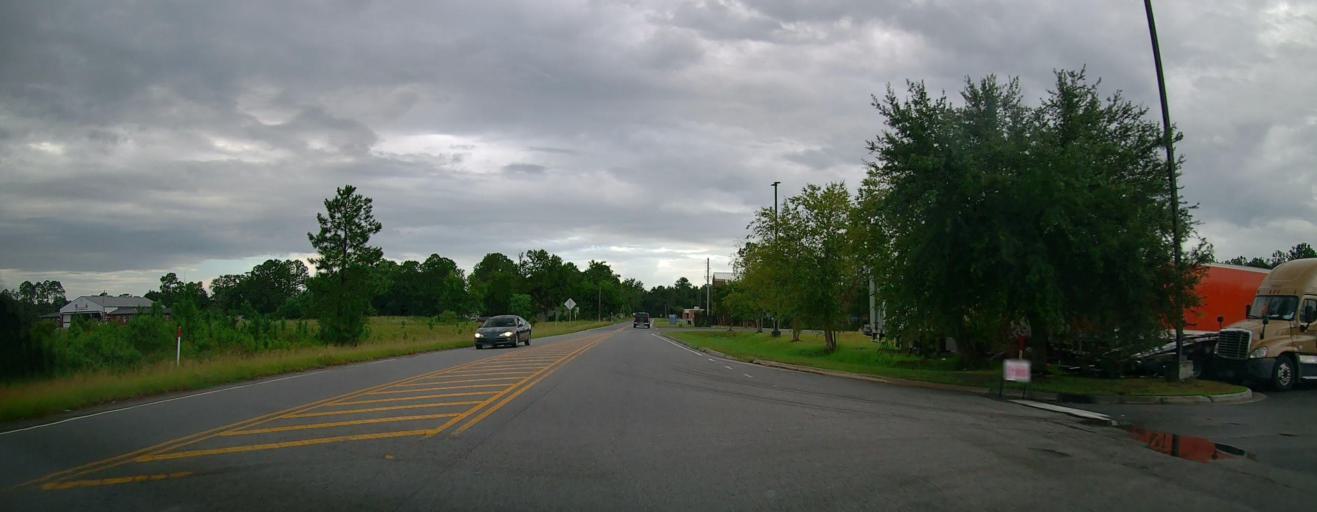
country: US
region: Georgia
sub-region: Ware County
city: Deenwood
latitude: 31.2098
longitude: -82.3837
